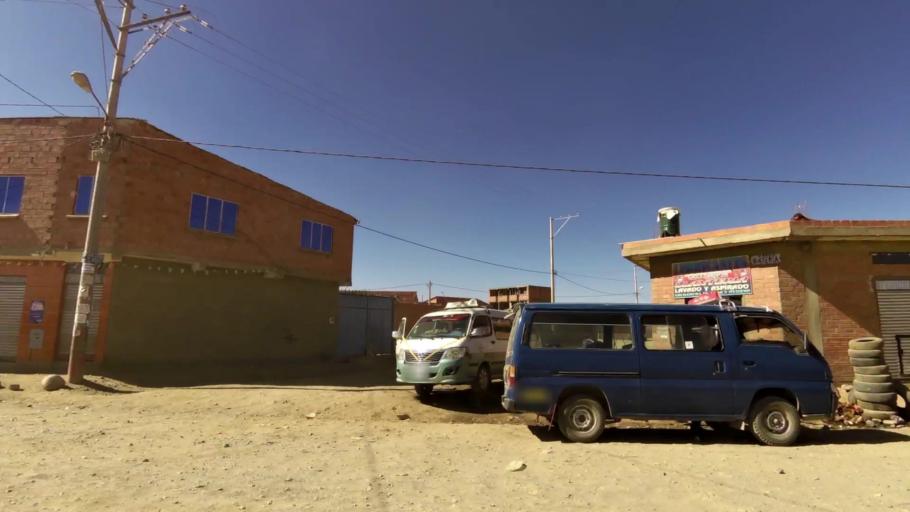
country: BO
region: La Paz
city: La Paz
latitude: -16.6214
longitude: -68.1861
